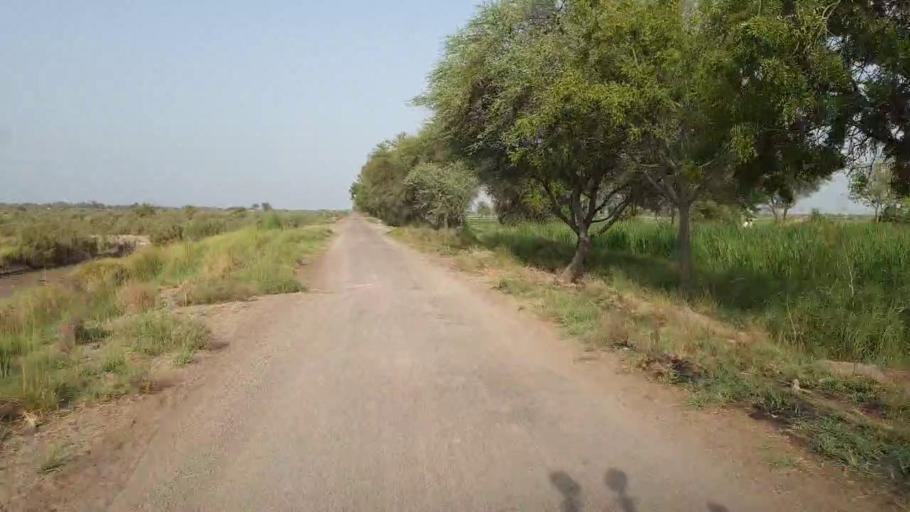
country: PK
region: Sindh
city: Daur
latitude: 26.3402
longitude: 68.2241
